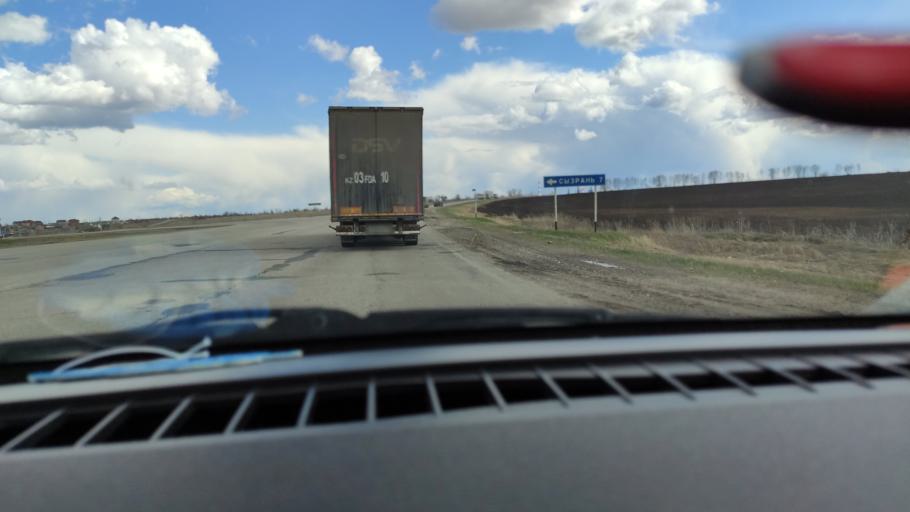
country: RU
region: Samara
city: Varlamovo
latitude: 53.1142
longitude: 48.3501
